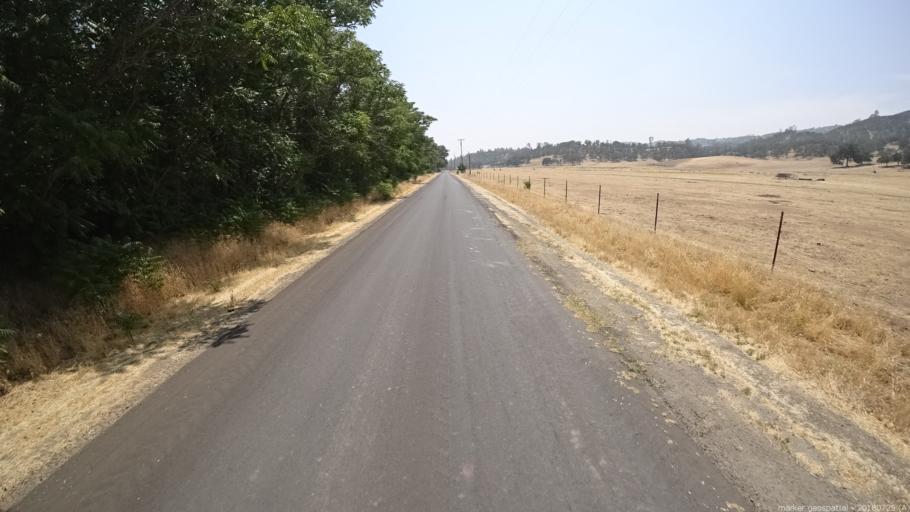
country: US
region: California
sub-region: Fresno County
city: Coalinga
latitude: 35.9514
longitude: -120.4741
